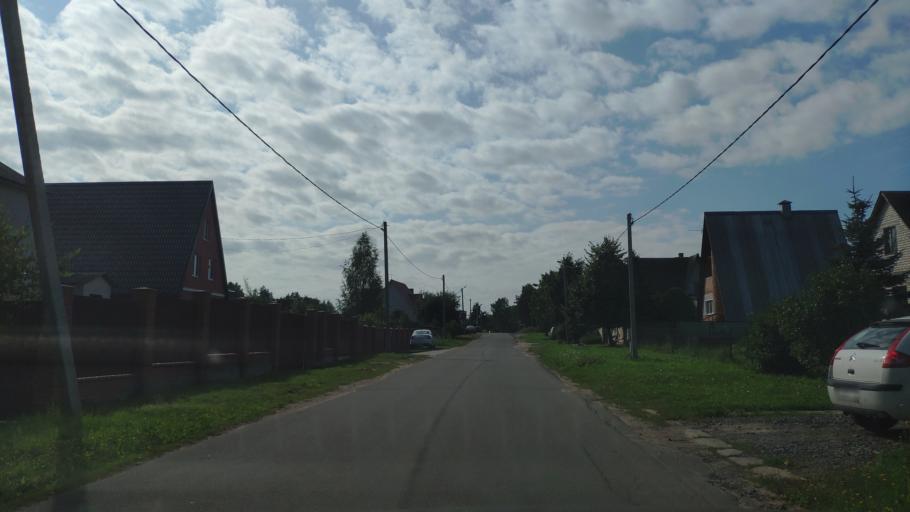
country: BY
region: Minsk
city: Zaslawye
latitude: 53.9949
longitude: 27.2828
